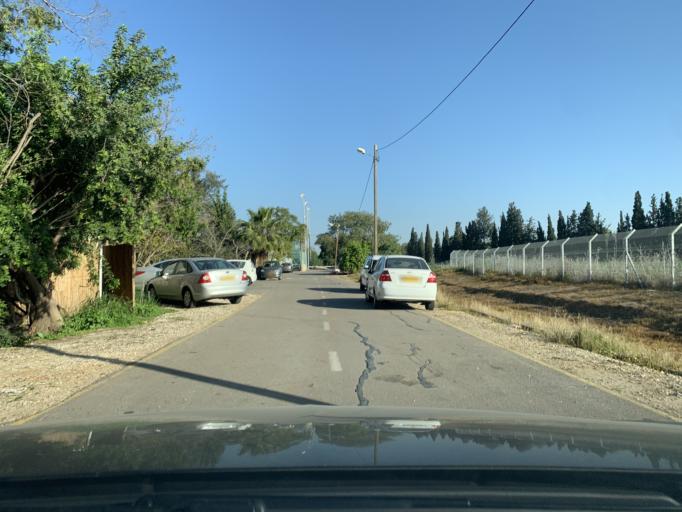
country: IL
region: Central District
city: Rosh Ha'Ayin
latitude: 32.1000
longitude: 34.9238
